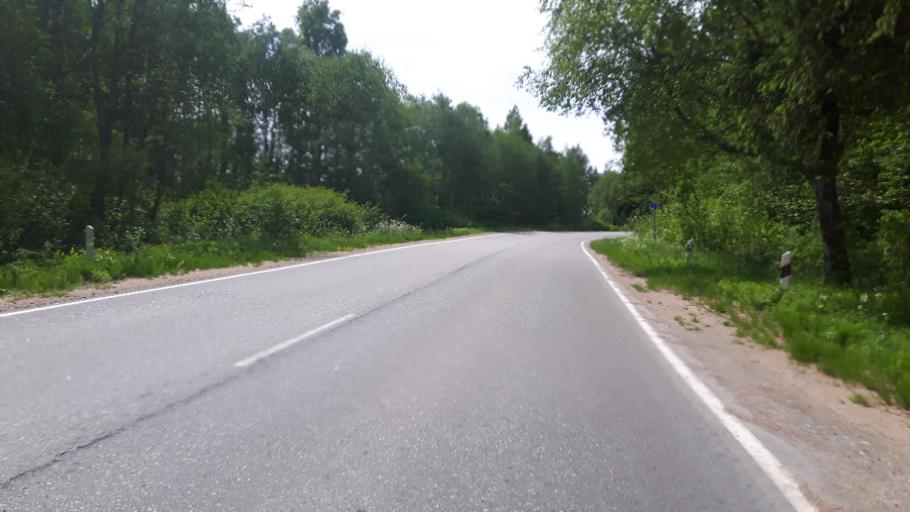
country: RU
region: Leningrad
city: Ust'-Luga
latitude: 59.6512
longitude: 28.2375
